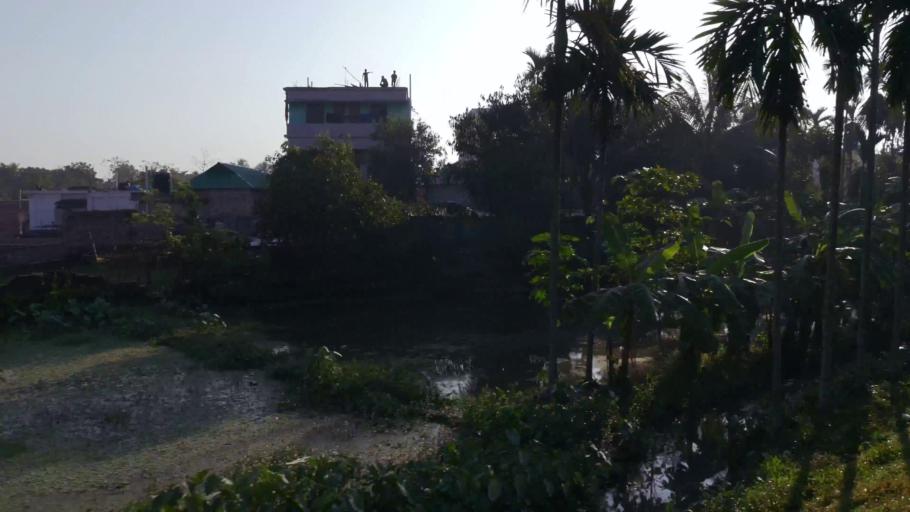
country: BD
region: Dhaka
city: Jamalpur
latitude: 24.9030
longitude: 89.9744
